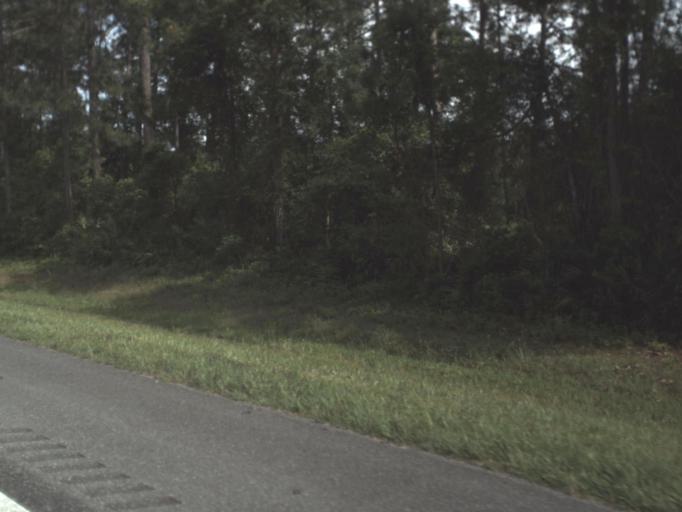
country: US
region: Florida
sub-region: Columbia County
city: Watertown
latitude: 30.2538
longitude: -82.4176
